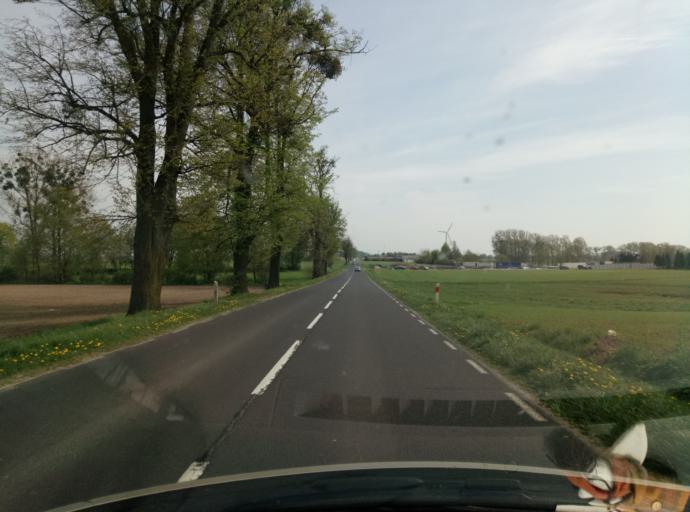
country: PL
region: Kujawsko-Pomorskie
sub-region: Powiat brodnicki
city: Jablonowo Pomorskie
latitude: 53.3847
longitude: 19.1093
